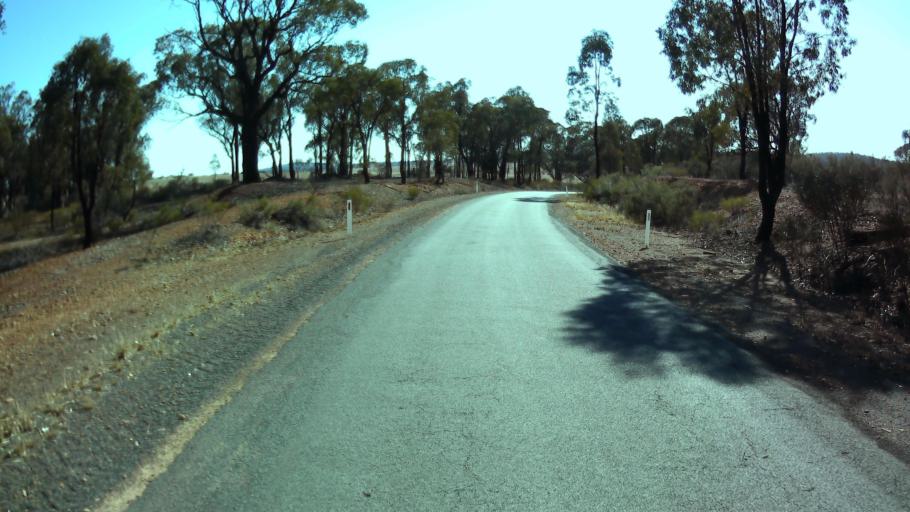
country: AU
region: New South Wales
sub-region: Weddin
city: Grenfell
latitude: -33.7824
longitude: 147.9612
